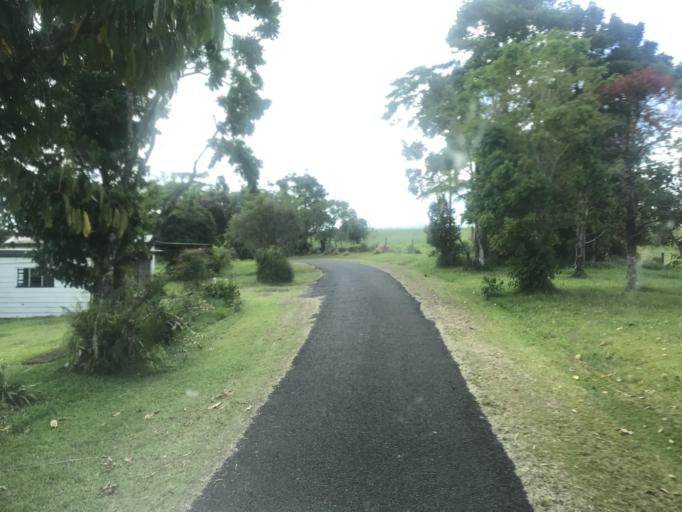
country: AU
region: Queensland
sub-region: Tablelands
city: Ravenshoe
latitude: -17.5547
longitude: 145.6921
